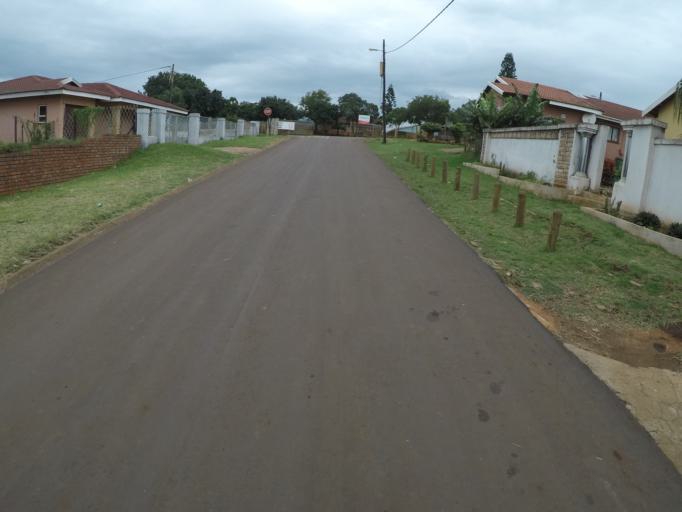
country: ZA
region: KwaZulu-Natal
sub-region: uThungulu District Municipality
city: Empangeni
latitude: -28.7766
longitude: 31.8512
